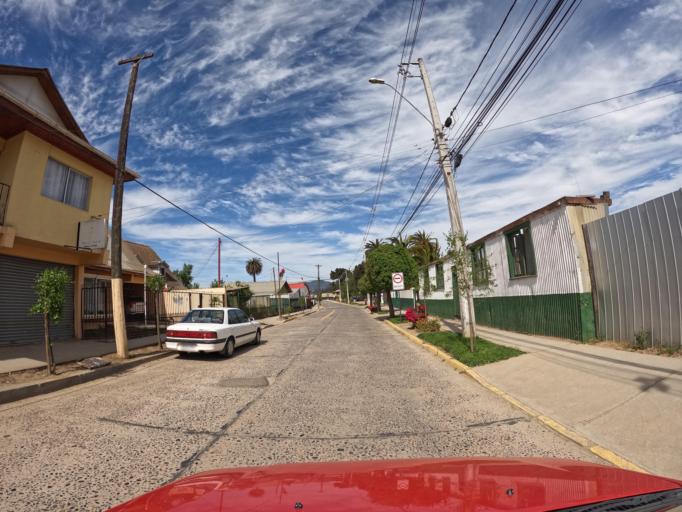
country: CL
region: Maule
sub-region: Provincia de Talca
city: Constitucion
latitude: -35.0912
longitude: -72.0205
